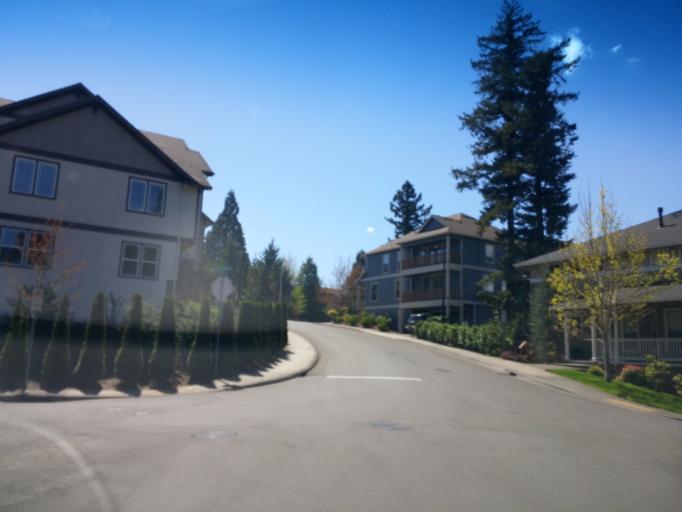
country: US
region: Oregon
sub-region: Washington County
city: West Haven
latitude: 45.5287
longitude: -122.7797
